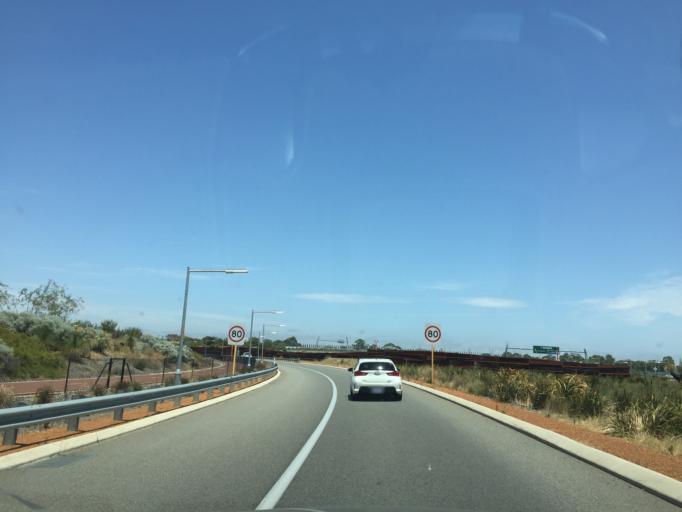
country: AU
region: Western Australia
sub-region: Belmont
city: Kewdale
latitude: -31.9634
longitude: 115.9593
